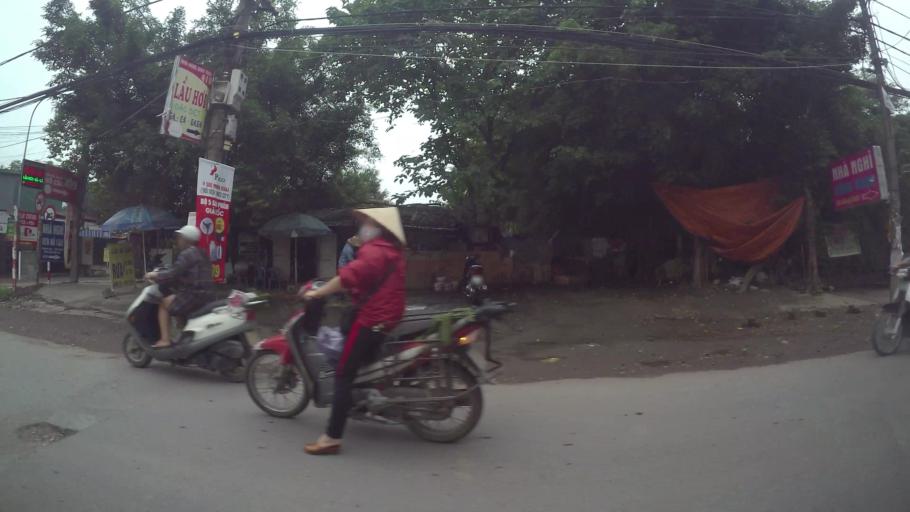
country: VN
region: Ha Noi
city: Hai BaTrung
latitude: 20.9824
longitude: 105.8788
